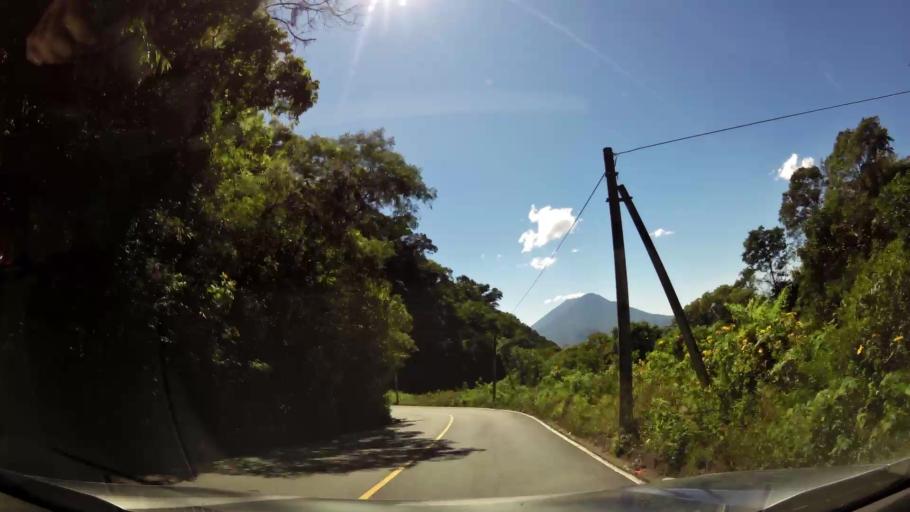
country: GT
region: Solola
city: Panajachel
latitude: 14.7562
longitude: -91.1617
